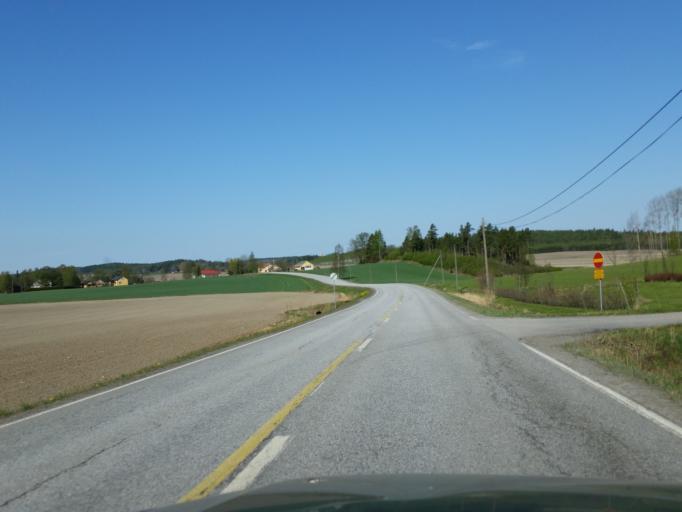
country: FI
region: Uusimaa
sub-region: Helsinki
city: Lohja
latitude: 60.1766
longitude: 24.0880
